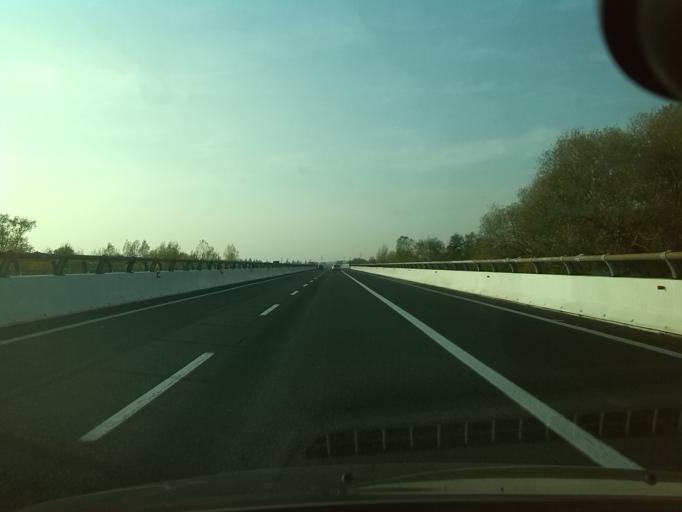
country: IT
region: Friuli Venezia Giulia
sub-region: Provincia di Gorizia
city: Villesse
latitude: 45.8535
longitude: 13.4512
